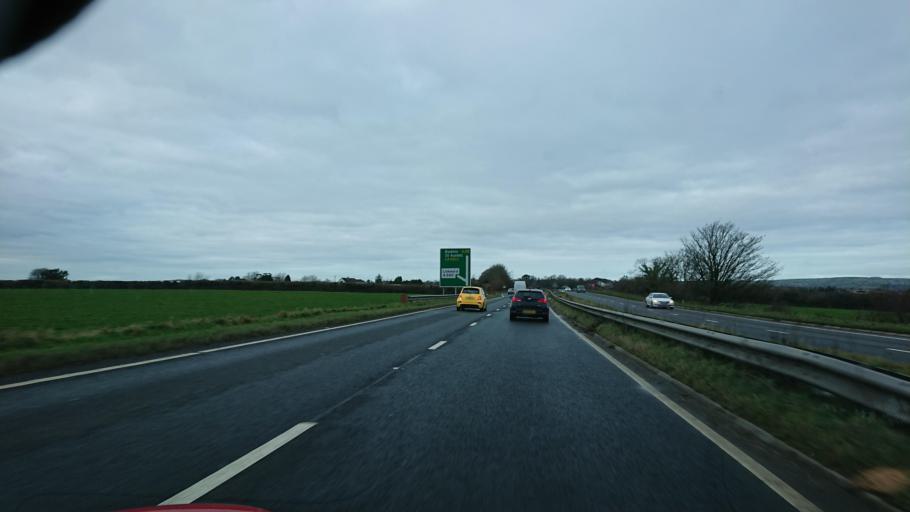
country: GB
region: England
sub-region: Cornwall
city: Liskeard
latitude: 50.4449
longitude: -4.4473
